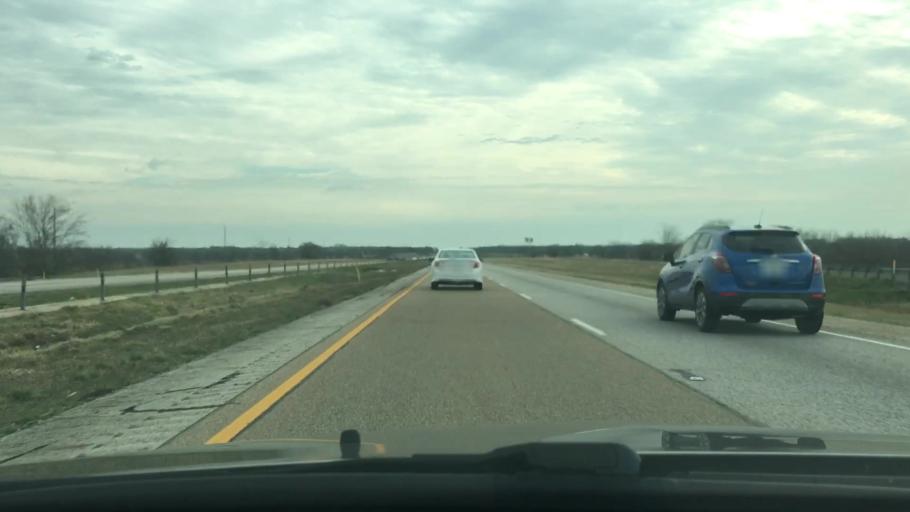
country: US
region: Texas
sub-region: Leon County
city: Centerville
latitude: 31.1026
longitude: -95.9646
